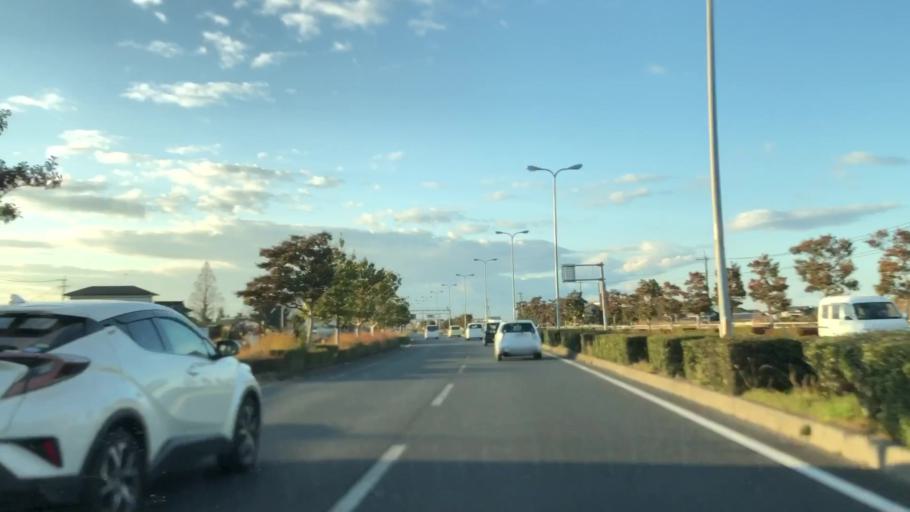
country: JP
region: Fukuoka
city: Nakatsu
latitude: 33.5439
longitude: 131.2868
